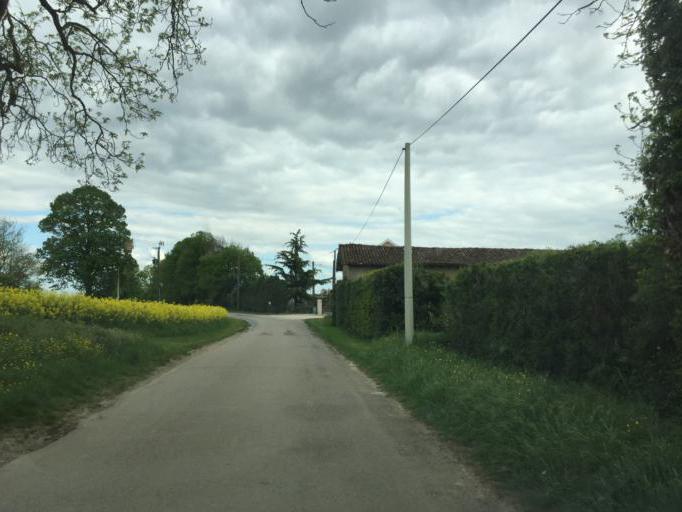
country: FR
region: Rhone-Alpes
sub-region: Departement de l'Ain
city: Tramoyes
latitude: 45.8975
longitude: 4.9735
